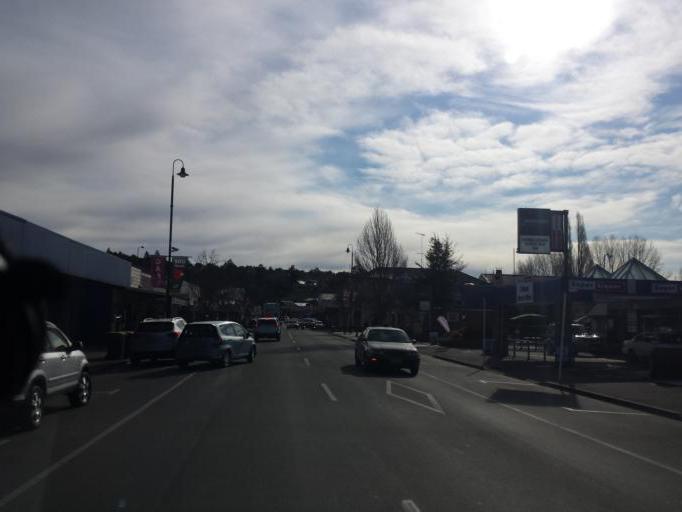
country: NZ
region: Canterbury
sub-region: Timaru District
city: Pleasant Point
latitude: -44.0920
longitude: 171.2445
